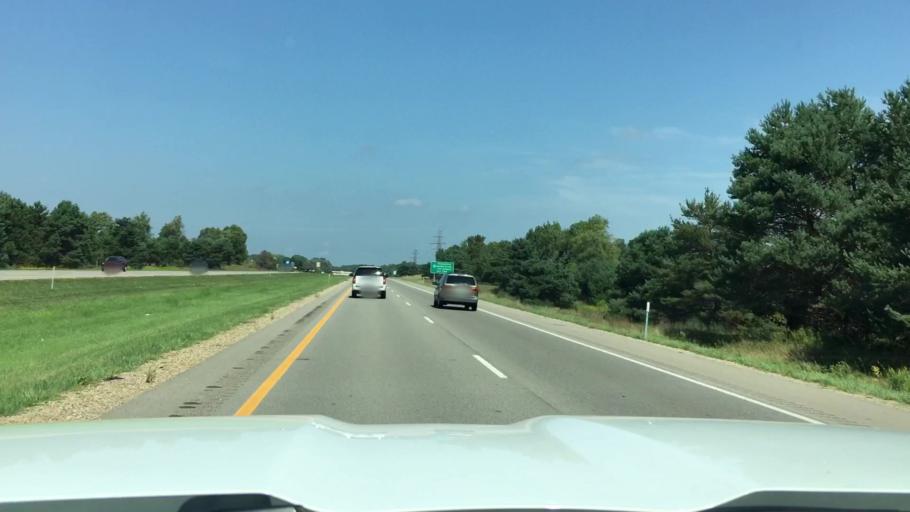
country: US
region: Michigan
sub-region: Kalamazoo County
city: Portage
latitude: 42.2193
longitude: -85.6411
